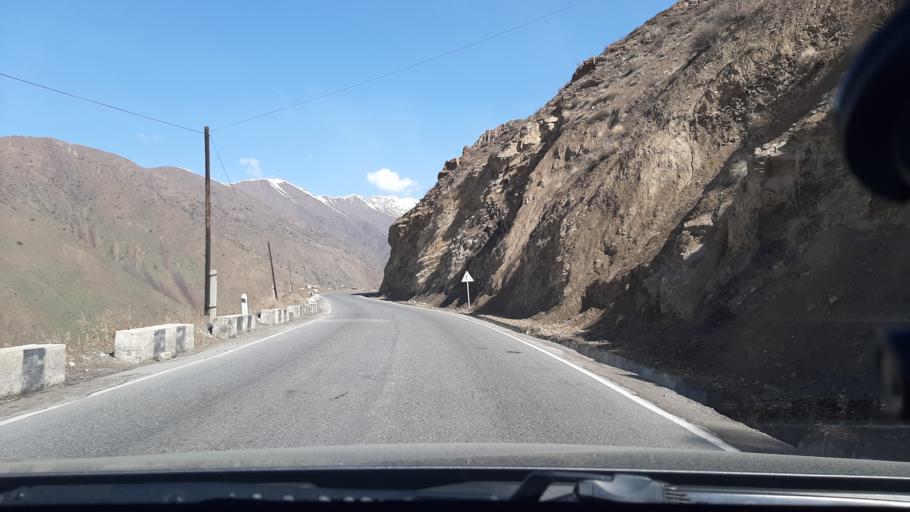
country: TJ
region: Viloyati Sughd
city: Ayni
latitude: 39.4410
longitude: 68.5495
